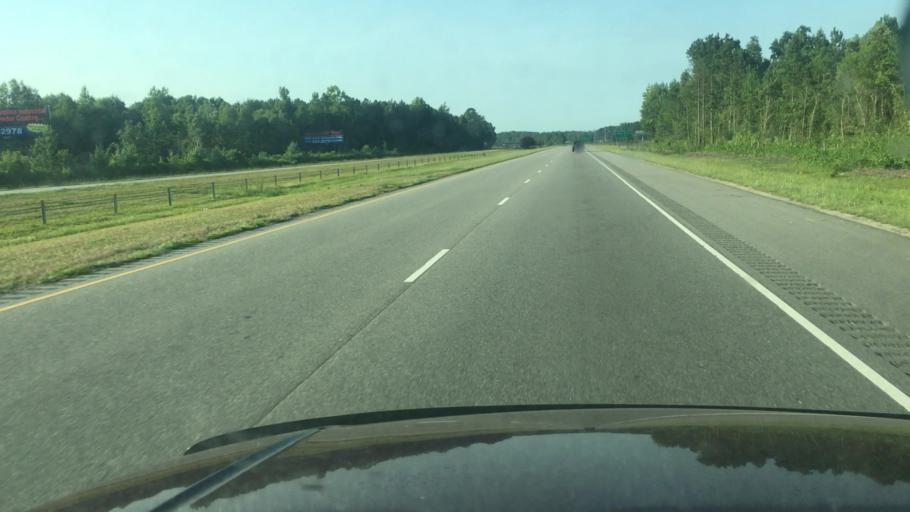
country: US
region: North Carolina
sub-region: Cumberland County
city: Fayetteville
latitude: 35.0225
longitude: -78.8721
